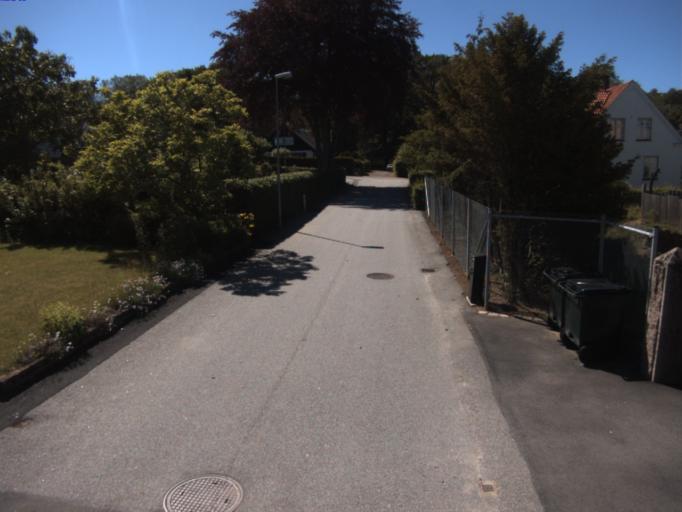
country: SE
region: Skane
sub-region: Helsingborg
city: Morarp
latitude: 56.0554
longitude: 12.8707
